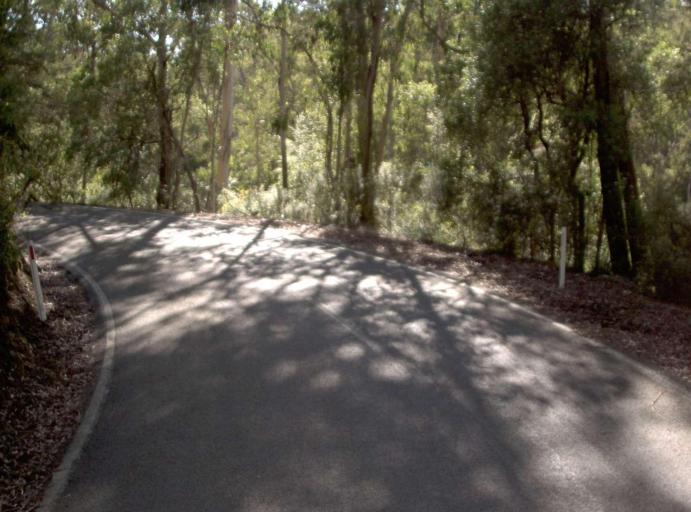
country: AU
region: Victoria
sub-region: East Gippsland
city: Lakes Entrance
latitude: -37.4825
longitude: 148.5556
